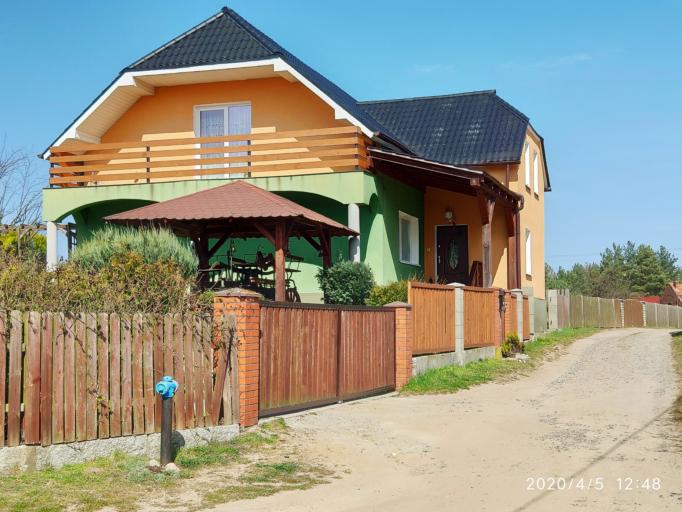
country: PL
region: Lubusz
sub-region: Powiat krosnienski
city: Dabie
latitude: 52.0301
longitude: 15.2461
